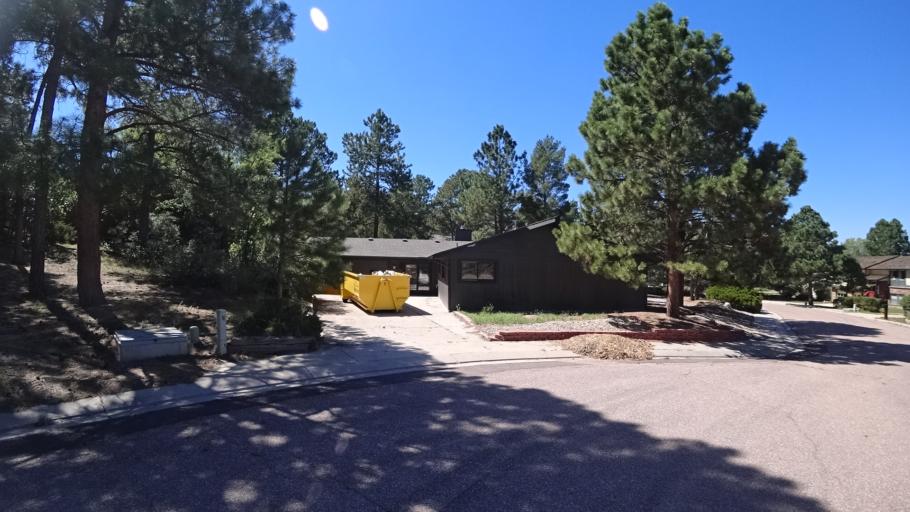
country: US
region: Colorado
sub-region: El Paso County
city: Colorado Springs
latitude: 38.9214
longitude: -104.7991
